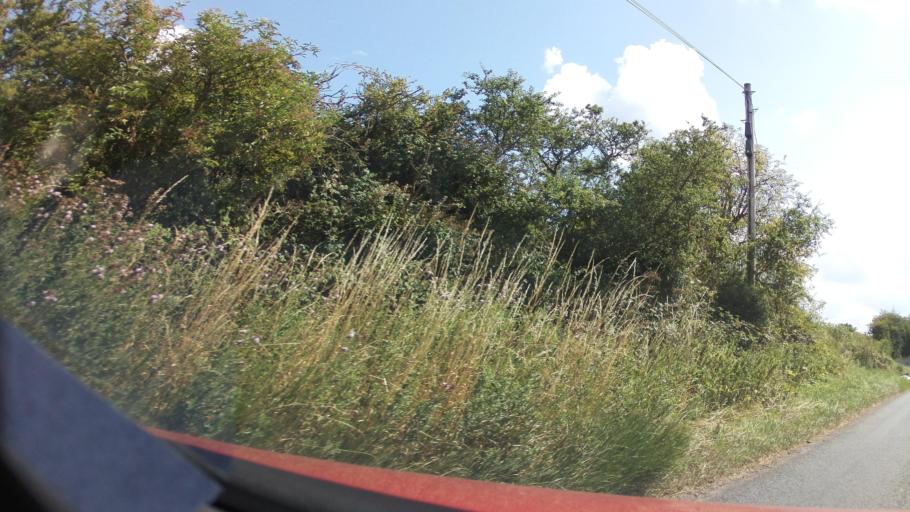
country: GB
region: England
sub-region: Wiltshire
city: Charlton
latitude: 51.5648
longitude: -2.0552
